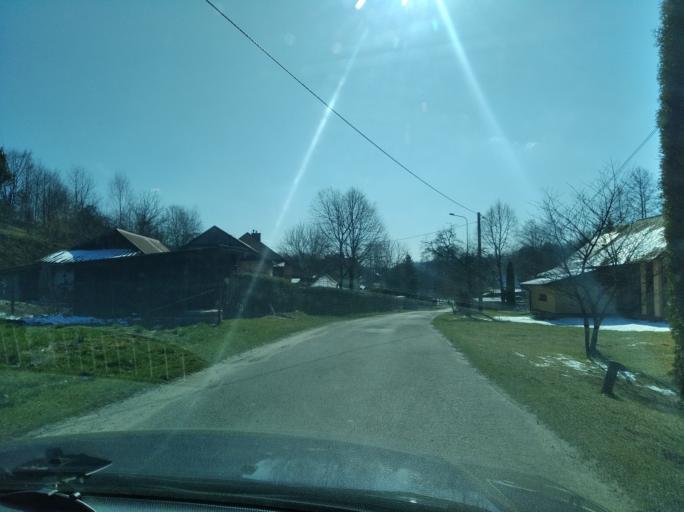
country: PL
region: Subcarpathian Voivodeship
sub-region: Powiat strzyzowski
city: Jawornik
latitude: 49.8514
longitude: 21.8694
